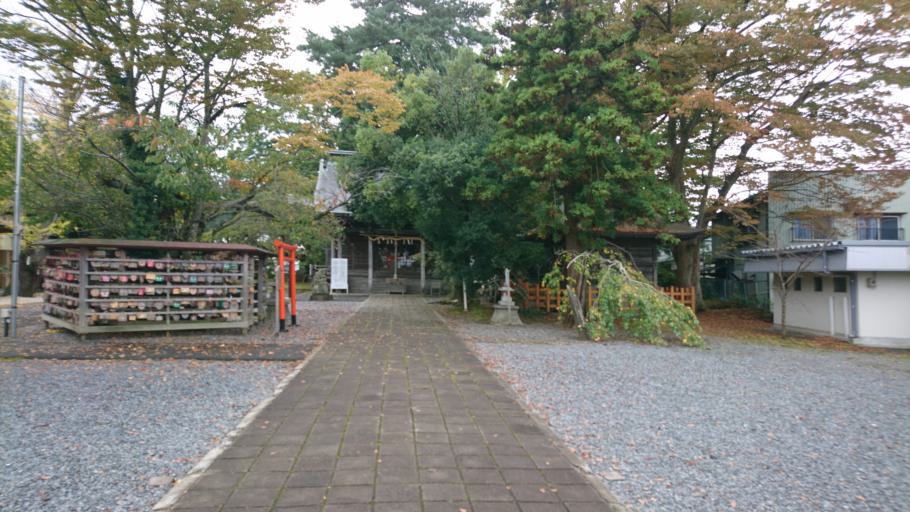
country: JP
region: Miyagi
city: Wakuya
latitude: 38.6847
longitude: 141.1969
